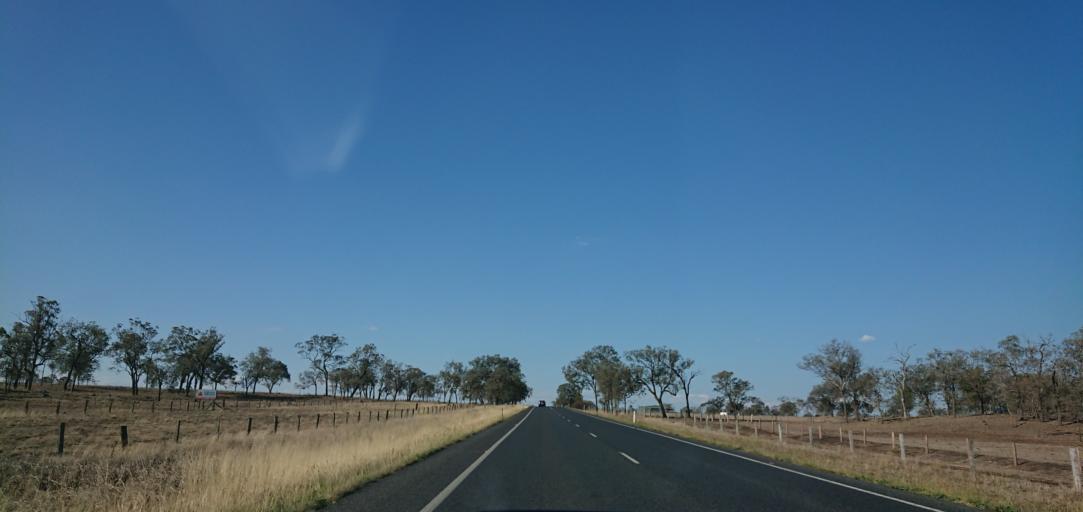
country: AU
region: Queensland
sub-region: Toowoomba
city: Westbrook
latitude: -27.6334
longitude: 151.7482
